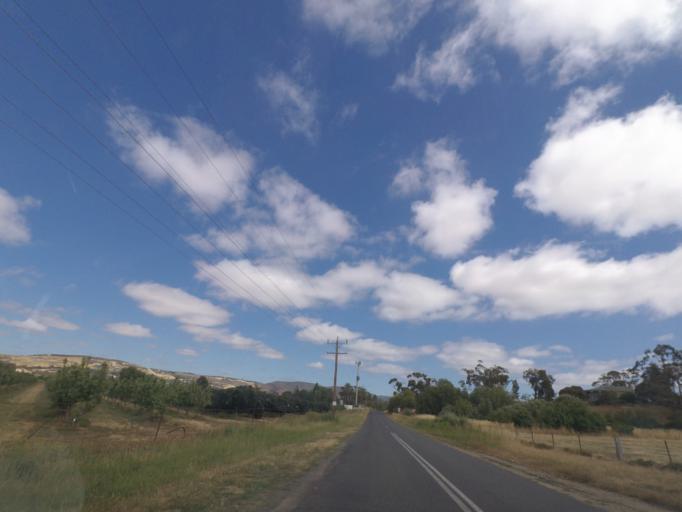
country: AU
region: Victoria
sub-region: Moorabool
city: Bacchus Marsh
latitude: -37.6513
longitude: 144.4515
